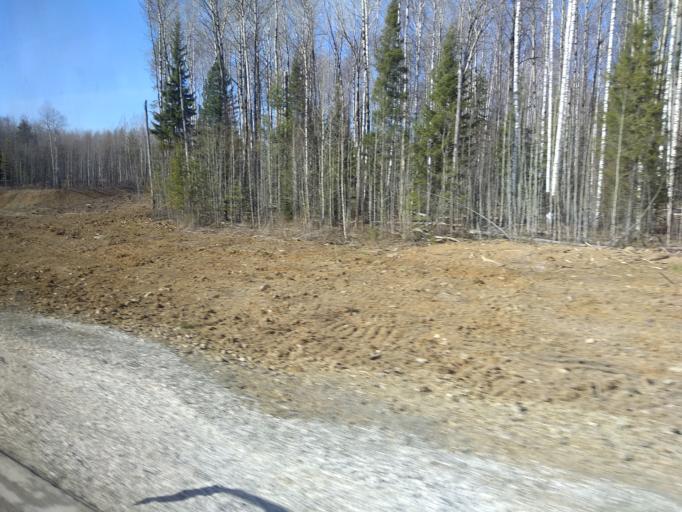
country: RU
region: Sverdlovsk
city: Krasnotur'insk
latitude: 59.6687
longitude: 60.1837
